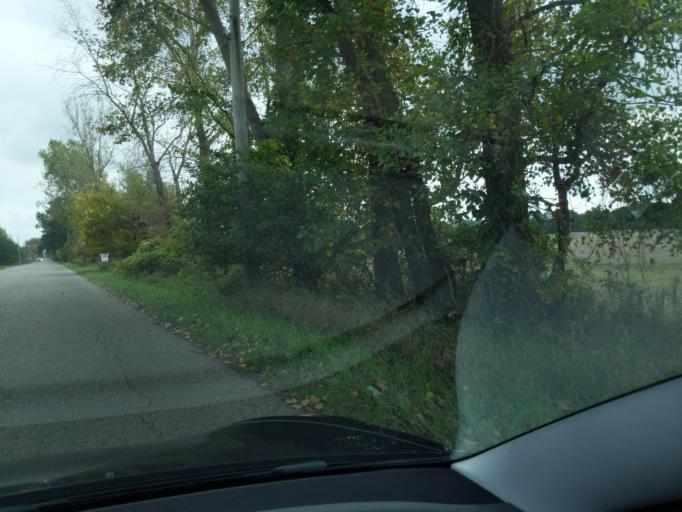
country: US
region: Michigan
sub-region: Eaton County
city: Eaton Rapids
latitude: 42.4923
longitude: -84.6535
